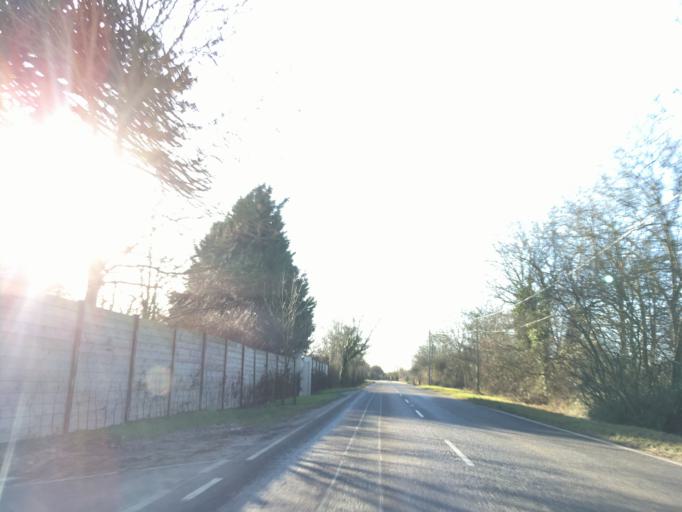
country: GB
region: England
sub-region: Wiltshire
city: Minety
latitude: 51.6177
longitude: -1.9480
